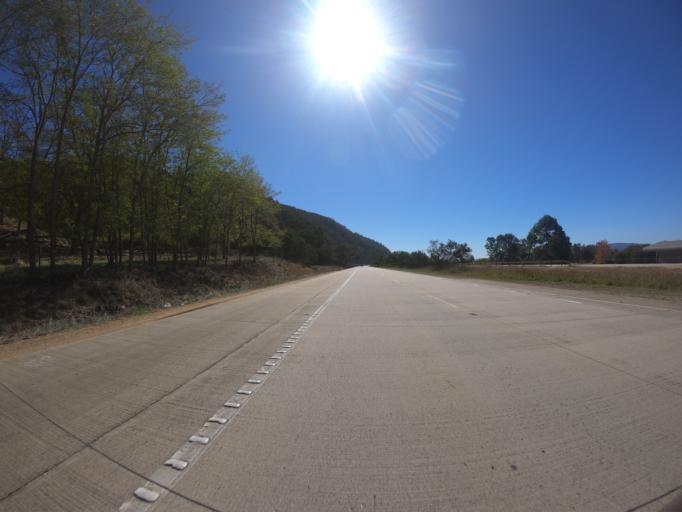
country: AU
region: New South Wales
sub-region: Yass Valley
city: Gundaroo
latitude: -35.0674
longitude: 149.3734
